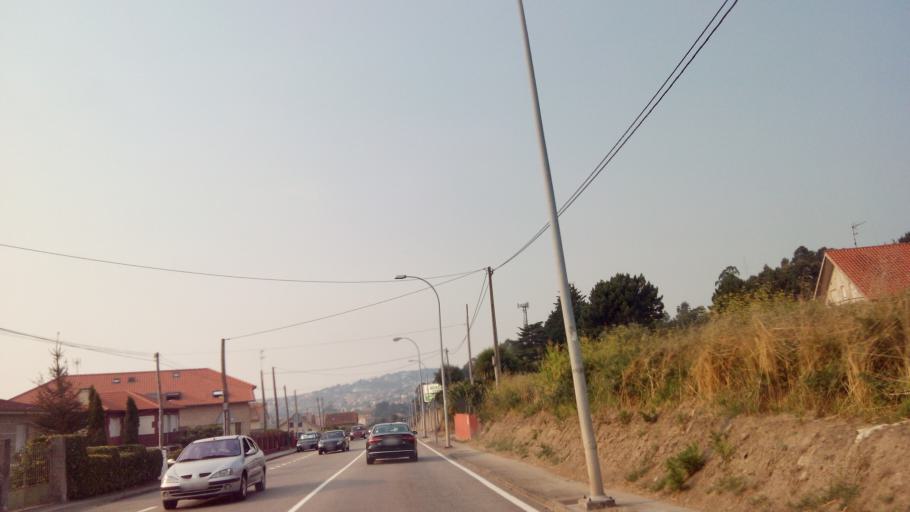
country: ES
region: Galicia
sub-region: Provincia de Pontevedra
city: Nigran
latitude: 42.1277
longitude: -8.8097
